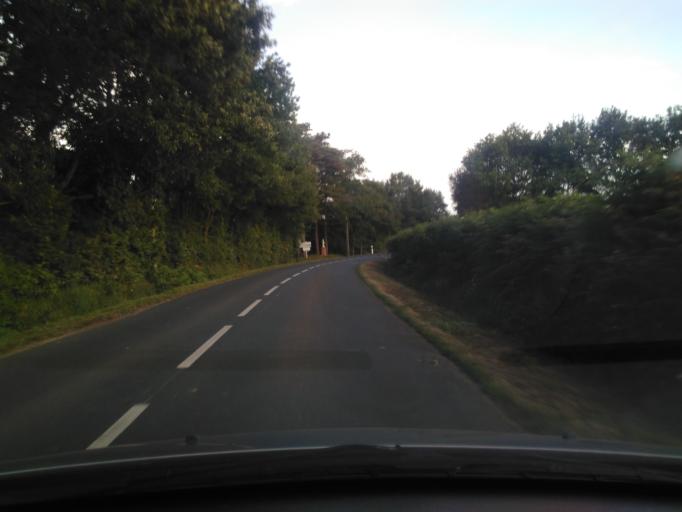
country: FR
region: Pays de la Loire
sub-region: Departement de la Vendee
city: Nesmy
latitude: 46.6012
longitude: -1.4038
